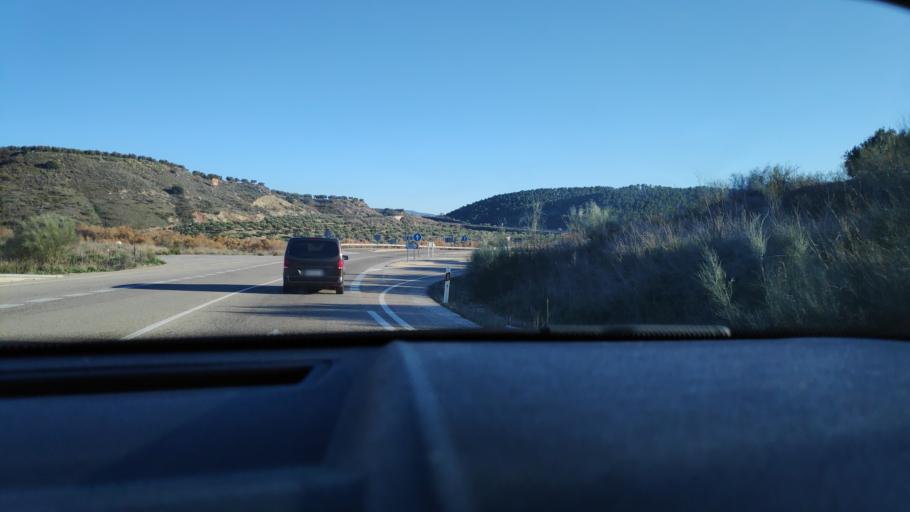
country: ES
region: Andalusia
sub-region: Province of Cordoba
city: Fuente-Tojar
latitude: 37.5795
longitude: -4.1608
